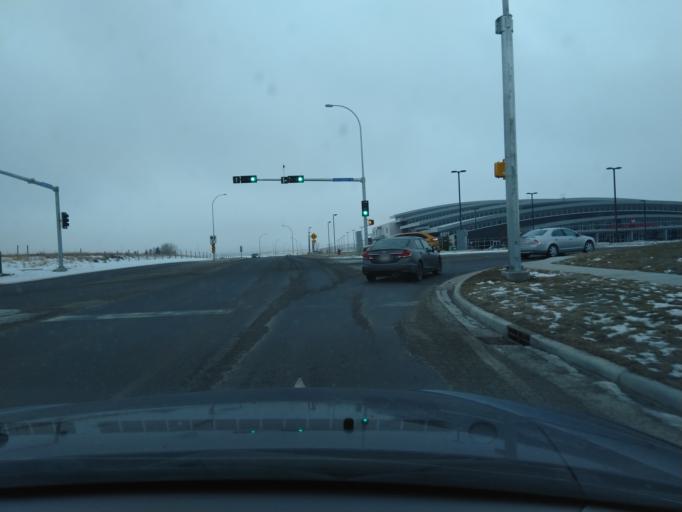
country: CA
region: Alberta
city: Airdrie
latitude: 51.1953
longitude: -113.9928
